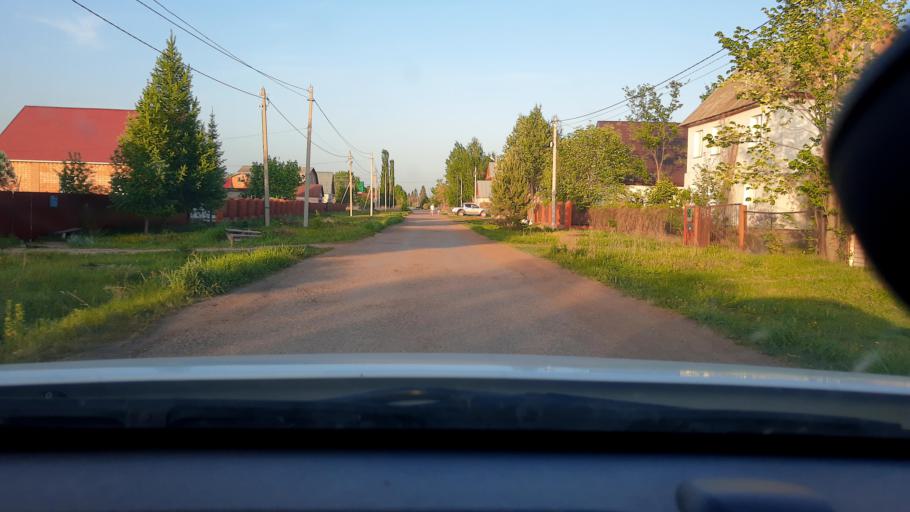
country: RU
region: Bashkortostan
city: Avdon
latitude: 54.4923
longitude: 55.8733
